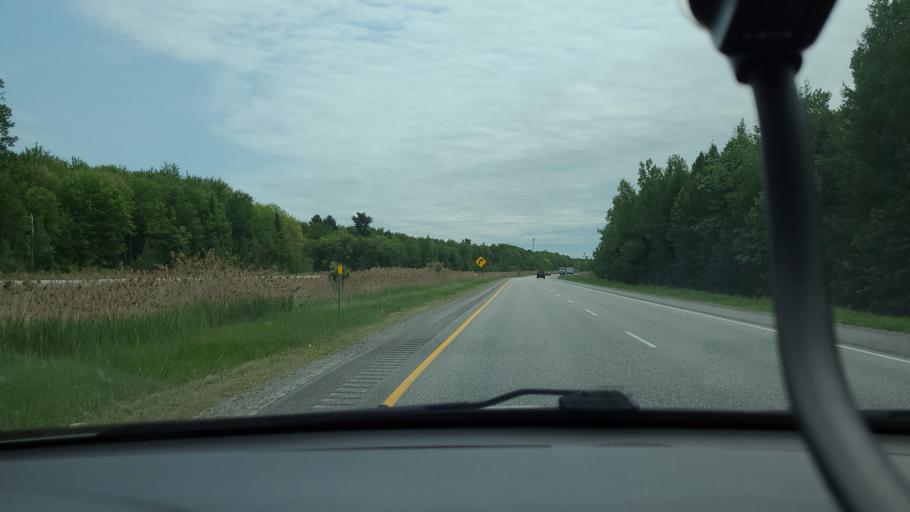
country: CA
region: Quebec
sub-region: Lanaudiere
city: Mascouche
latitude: 45.8149
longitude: -73.5971
